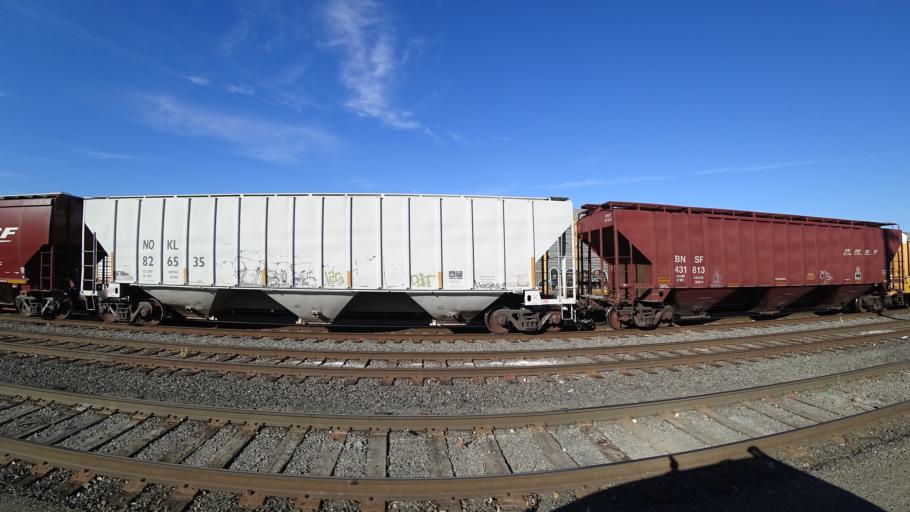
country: US
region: Oregon
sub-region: Multnomah County
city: Portland
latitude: 45.5476
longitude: -122.6911
